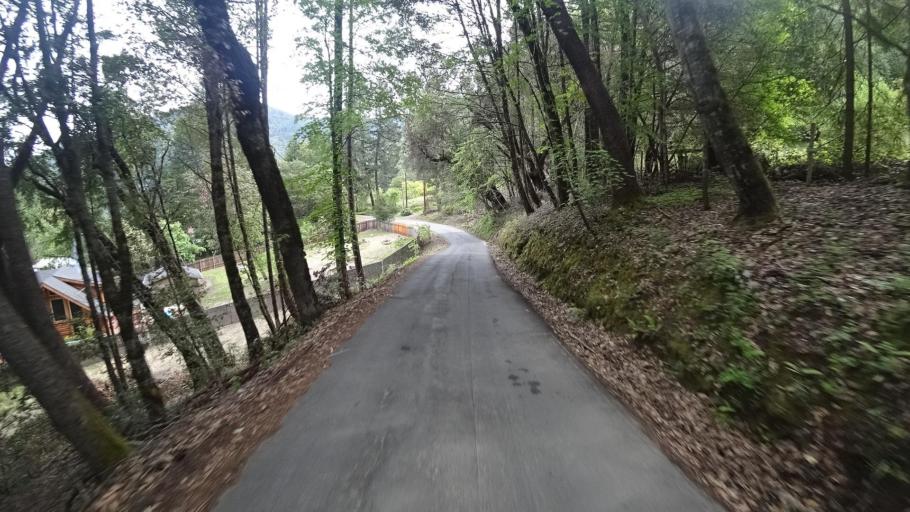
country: US
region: California
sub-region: Humboldt County
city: Willow Creek
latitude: 40.9385
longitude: -123.6148
